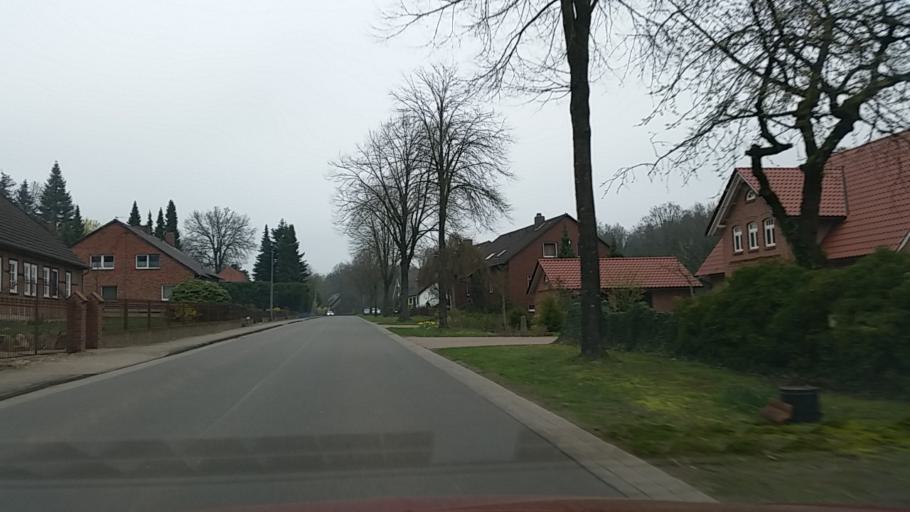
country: DE
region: Lower Saxony
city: Hankensbuttel
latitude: 52.6804
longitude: 10.5752
